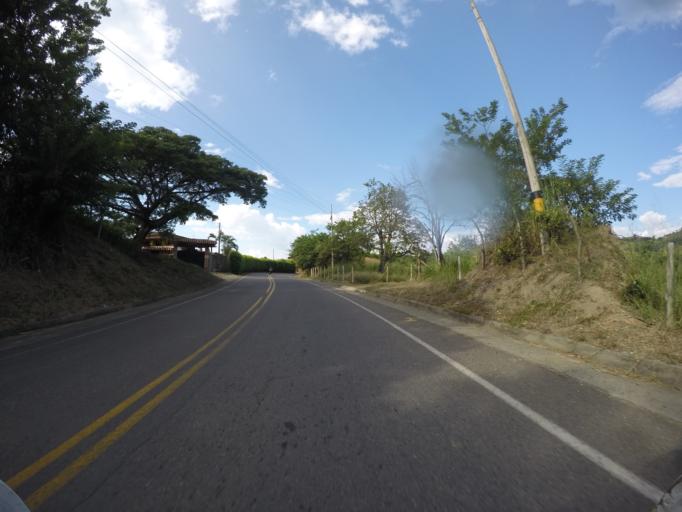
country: CO
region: Valle del Cauca
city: Cartago
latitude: 4.7259
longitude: -75.8794
